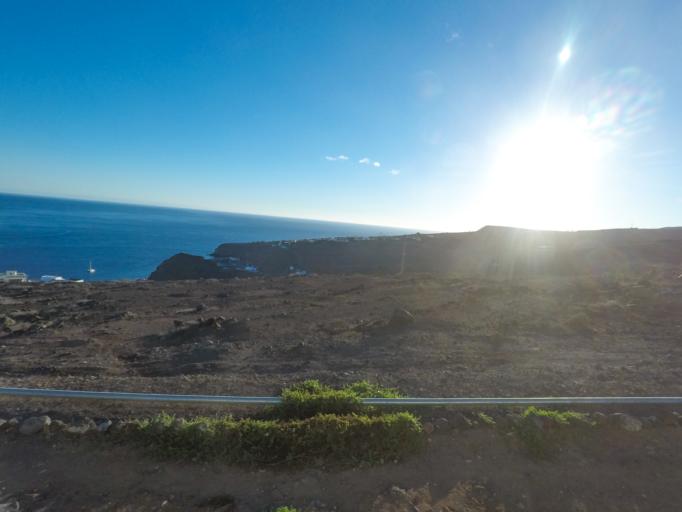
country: ES
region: Canary Islands
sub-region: Provincia de Santa Cruz de Tenerife
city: Alajero
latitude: 28.0375
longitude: -17.1947
